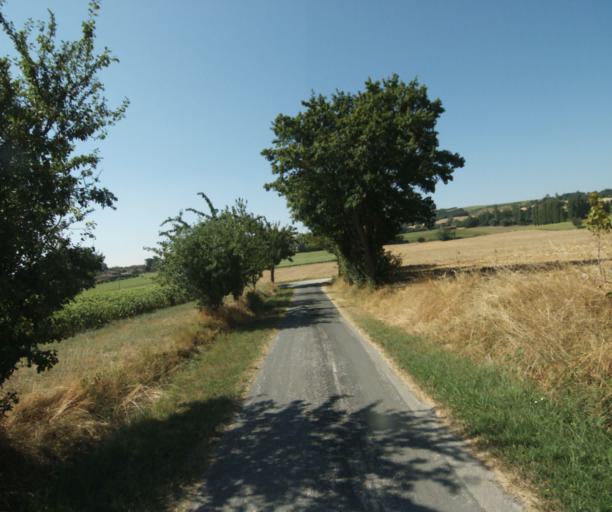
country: FR
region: Midi-Pyrenees
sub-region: Departement de la Haute-Garonne
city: Revel
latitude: 43.5097
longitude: 1.9484
